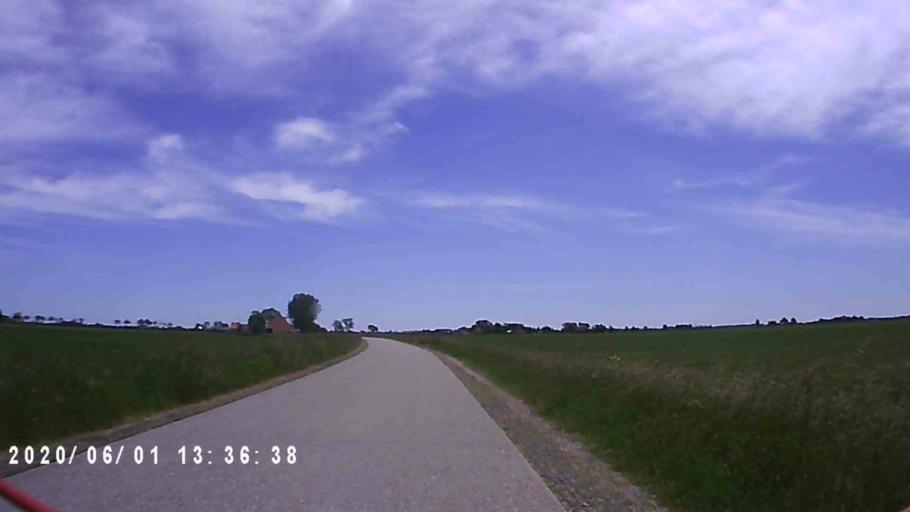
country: NL
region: Friesland
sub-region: Gemeente Littenseradiel
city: Wommels
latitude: 53.0860
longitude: 5.5885
